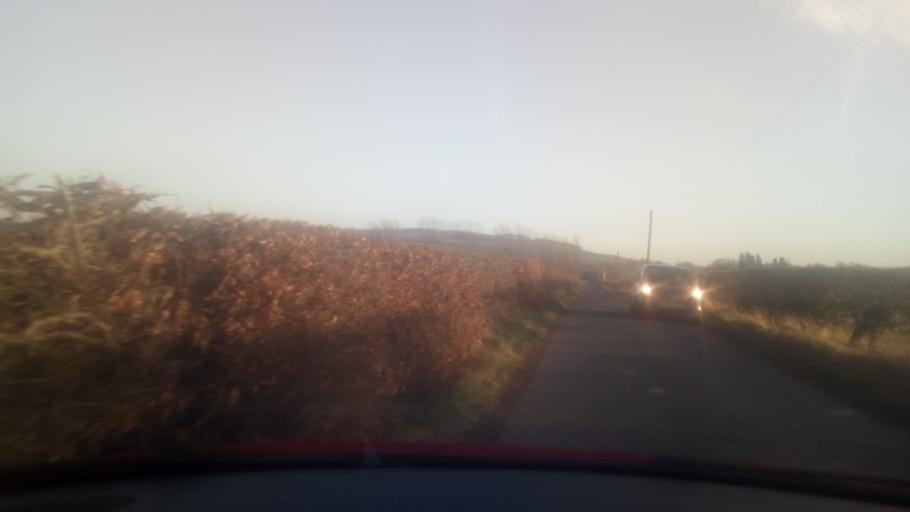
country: GB
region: Scotland
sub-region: The Scottish Borders
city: Jedburgh
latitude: 55.5198
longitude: -2.5144
